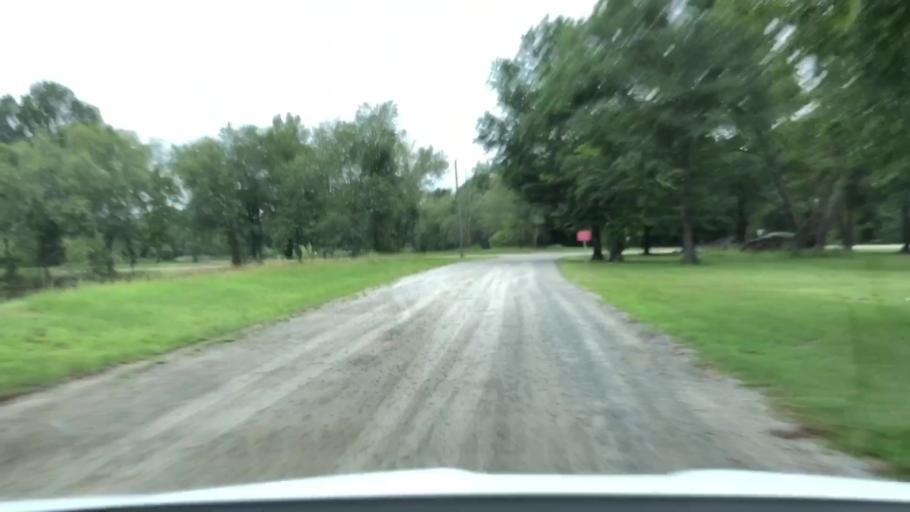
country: US
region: North Carolina
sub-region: Lenoir County
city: Kinston
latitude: 35.2595
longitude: -77.5932
